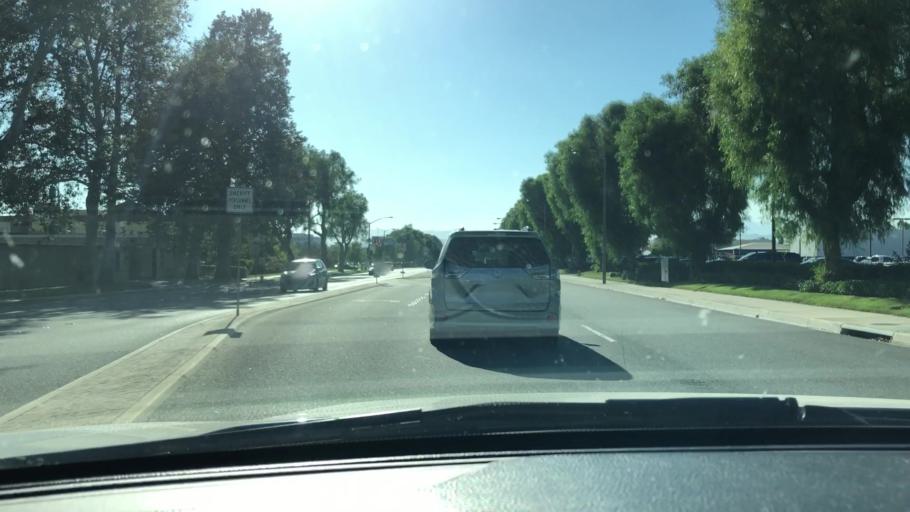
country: US
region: California
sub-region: Los Angeles County
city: Santa Clarita
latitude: 34.4164
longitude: -118.5512
